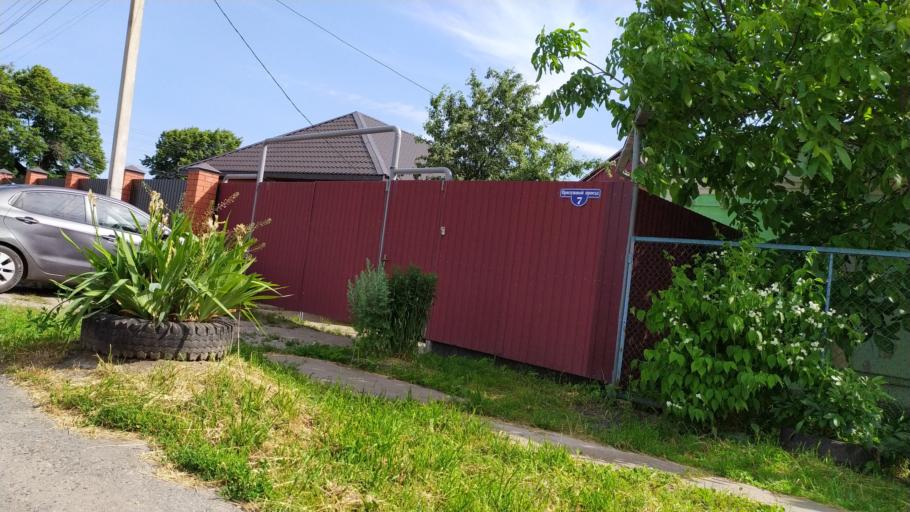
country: RU
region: Kursk
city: Kursk
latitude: 51.6622
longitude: 36.1534
